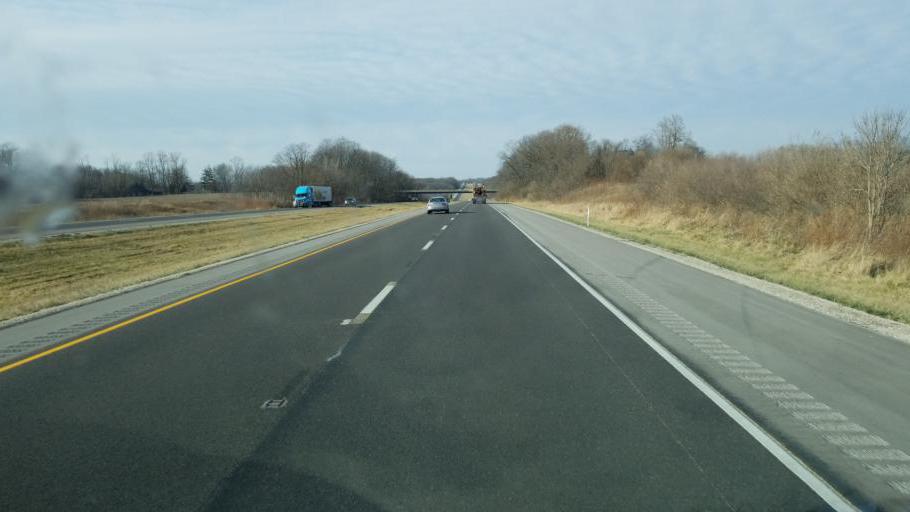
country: US
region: Illinois
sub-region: Peoria County
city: Elmwood
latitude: 40.8564
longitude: -89.9993
